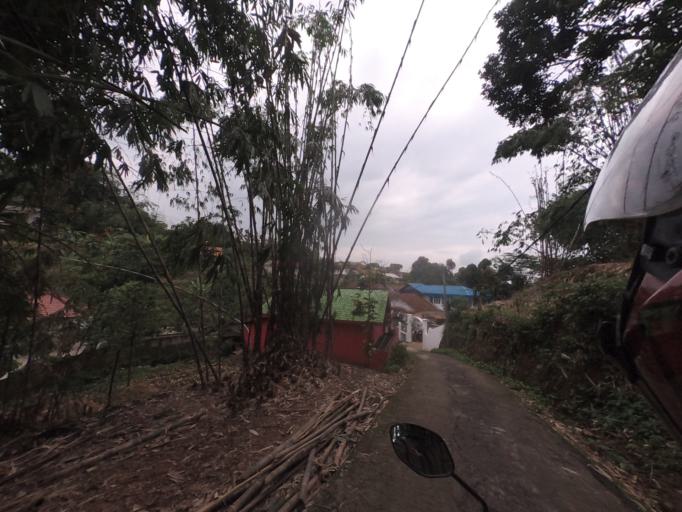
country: ID
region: West Java
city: Bogor
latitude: -6.6152
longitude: 106.7338
